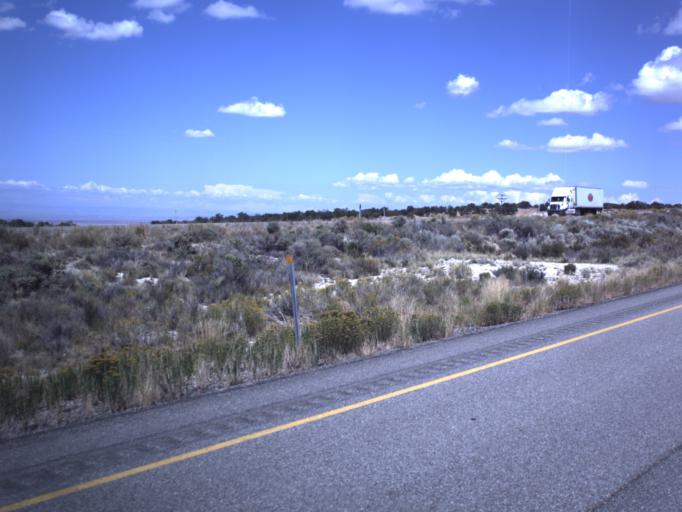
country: US
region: Utah
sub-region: Emery County
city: Ferron
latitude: 38.8482
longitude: -110.9315
